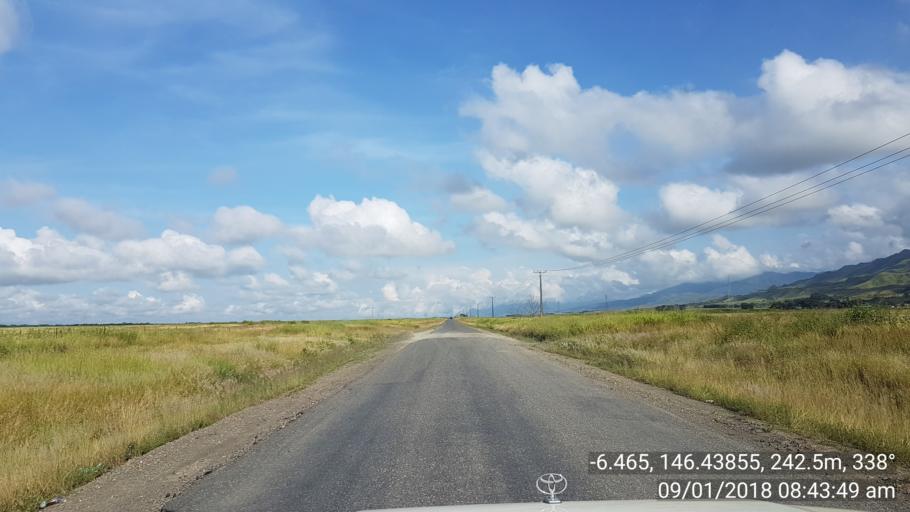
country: PG
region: Eastern Highlands
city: Kainantu
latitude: -6.4649
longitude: 146.4388
